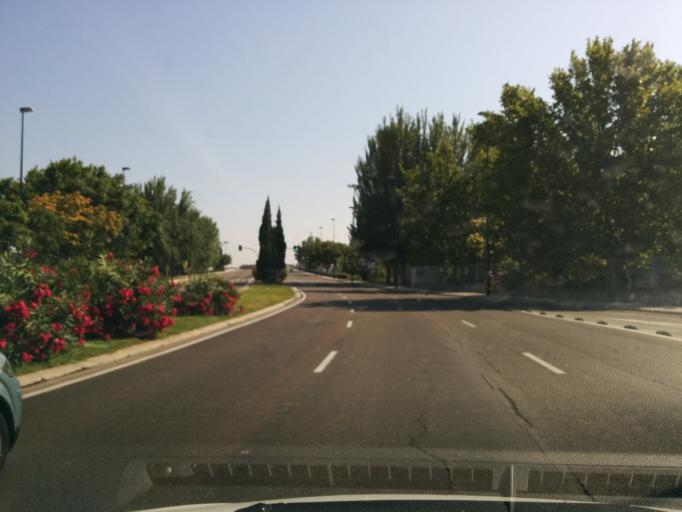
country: ES
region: Aragon
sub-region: Provincia de Zaragoza
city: Zaragoza
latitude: 41.6495
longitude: -0.8645
